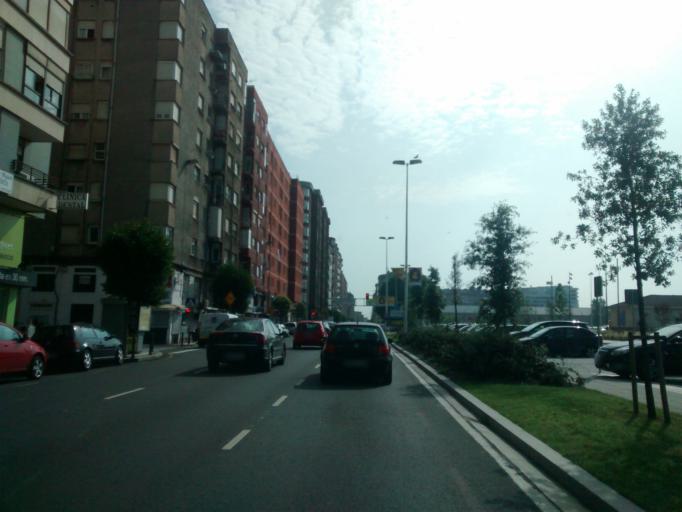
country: ES
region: Cantabria
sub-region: Provincia de Cantabria
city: Santander
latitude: 43.4537
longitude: -3.8198
